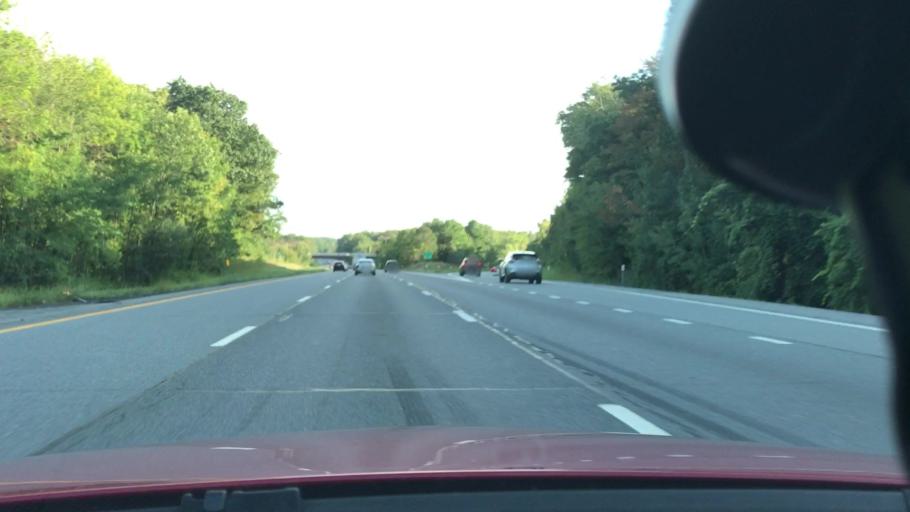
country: US
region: New York
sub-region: Saratoga County
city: Country Knolls
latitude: 42.8444
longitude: -73.7732
